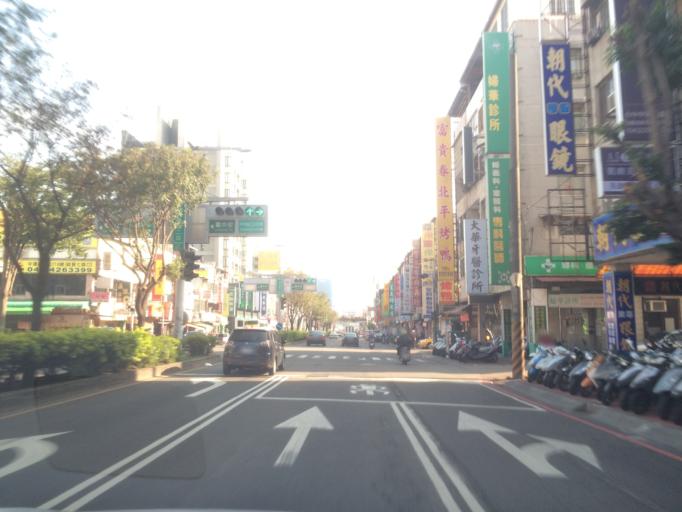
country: TW
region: Taiwan
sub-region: Taichung City
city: Taichung
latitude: 24.1802
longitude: 120.6671
